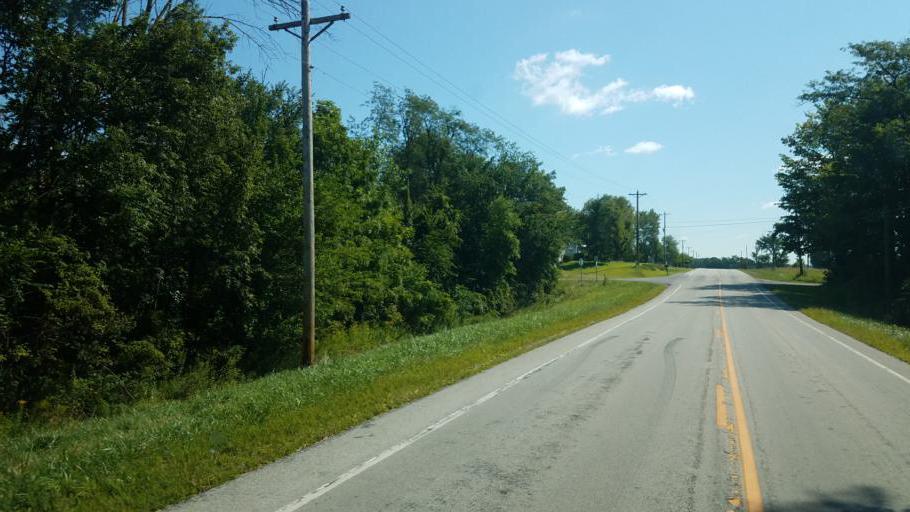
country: US
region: Ohio
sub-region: Wyandot County
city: Carey
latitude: 40.9478
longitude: -83.3347
